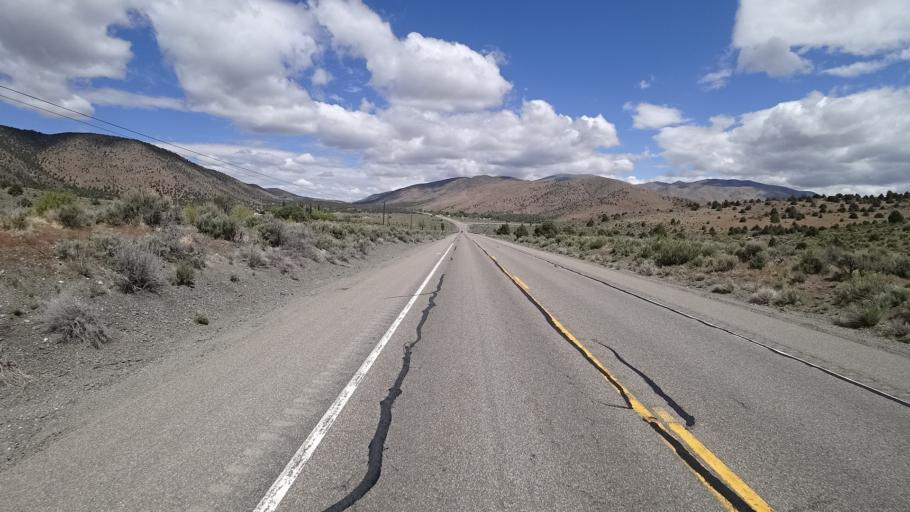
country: US
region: Nevada
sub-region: Lyon County
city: Smith Valley
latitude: 38.7181
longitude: -119.5541
